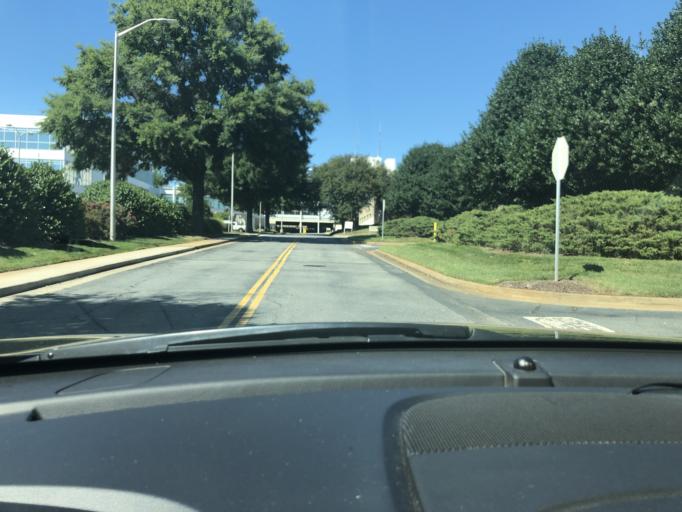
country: US
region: Georgia
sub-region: Gwinnett County
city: Lawrenceville
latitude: 33.9616
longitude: -84.0177
